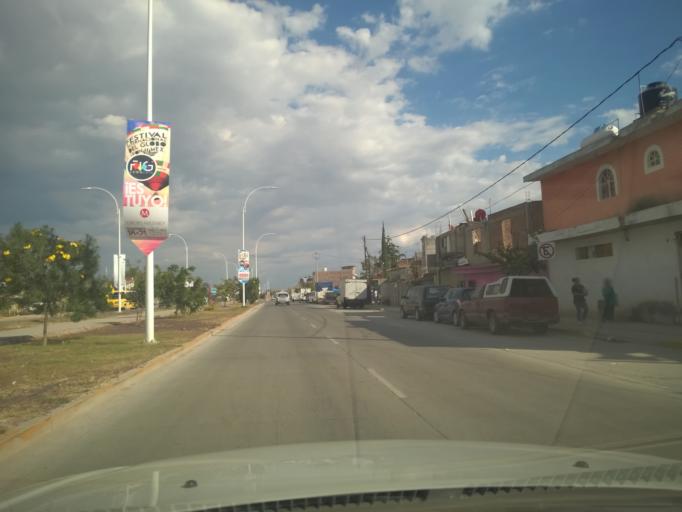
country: MX
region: Guanajuato
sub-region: Leon
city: San Jose de Duran (Los Troncoso)
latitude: 21.0643
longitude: -101.6305
